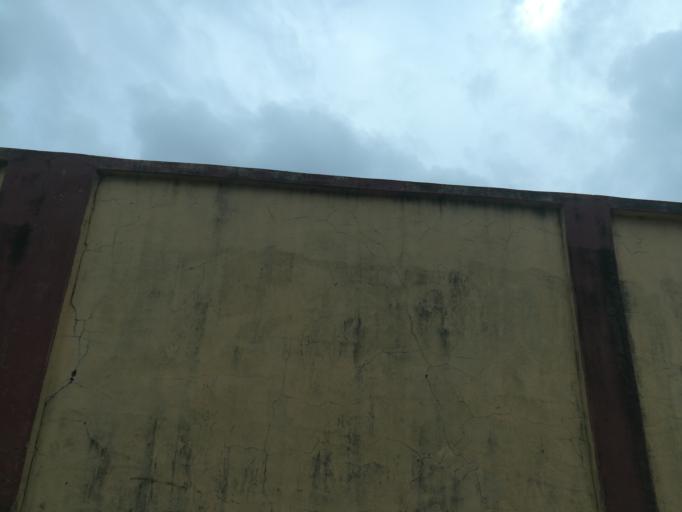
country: NG
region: Lagos
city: Oshodi
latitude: 6.5626
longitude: 3.3449
